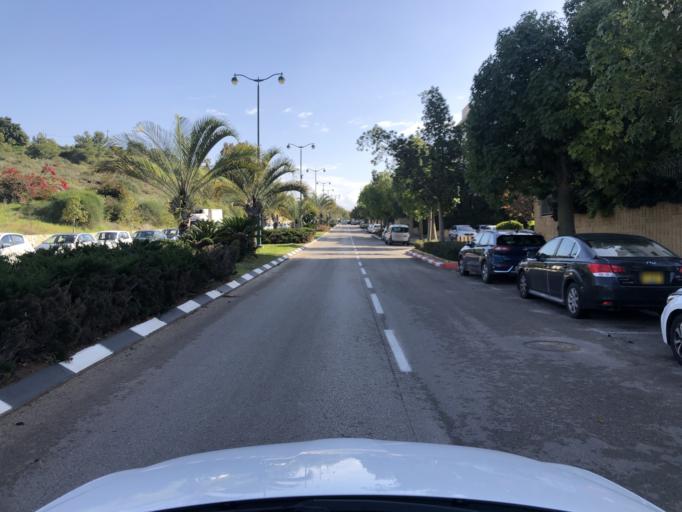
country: IL
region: Central District
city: Ness Ziona
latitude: 31.9148
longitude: 34.7893
